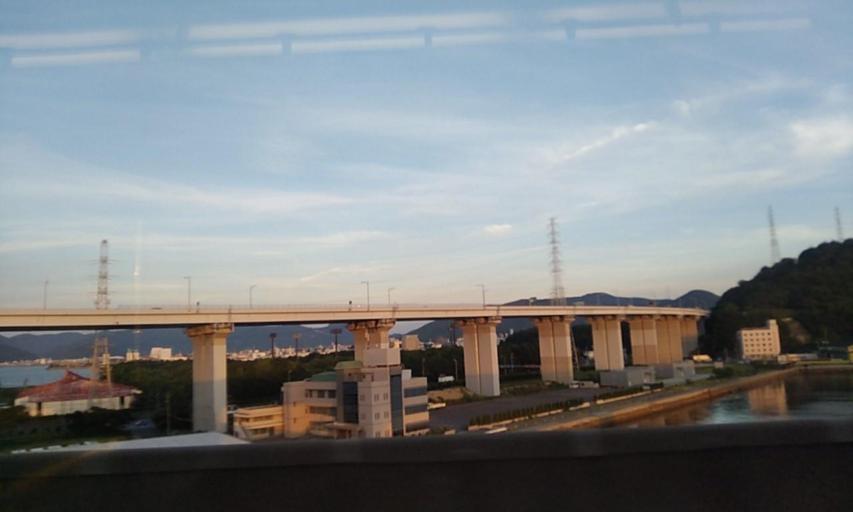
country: JP
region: Kagawa
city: Sakaidecho
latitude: 34.3265
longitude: 133.8262
